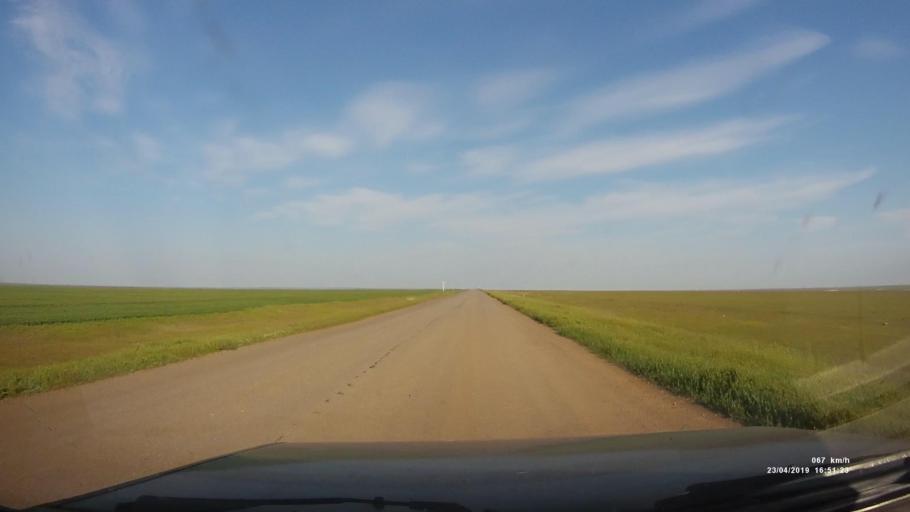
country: RU
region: Kalmykiya
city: Priyutnoye
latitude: 46.3233
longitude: 43.3053
